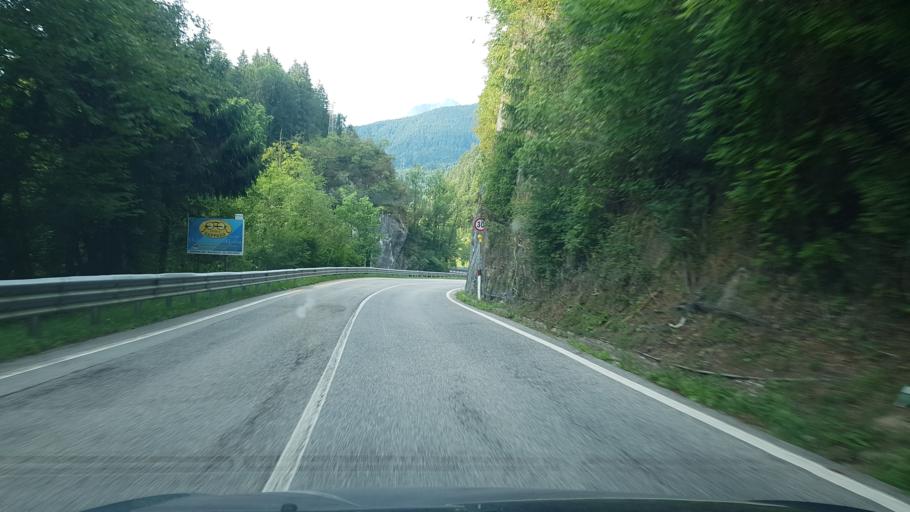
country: IT
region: Friuli Venezia Giulia
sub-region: Provincia di Udine
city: Comeglians
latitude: 46.5189
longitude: 12.8673
